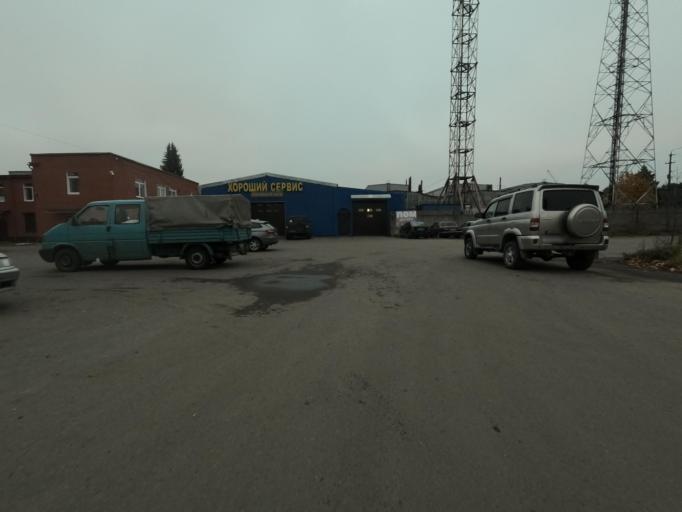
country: RU
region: Leningrad
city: Kirovsk
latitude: 59.8899
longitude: 30.9935
